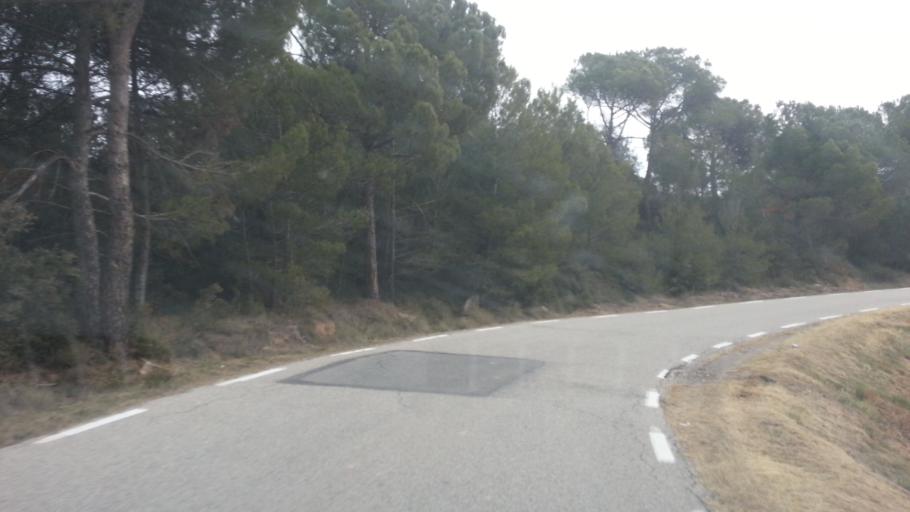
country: ES
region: Catalonia
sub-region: Provincia de Barcelona
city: Navas
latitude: 41.9078
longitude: 1.8552
